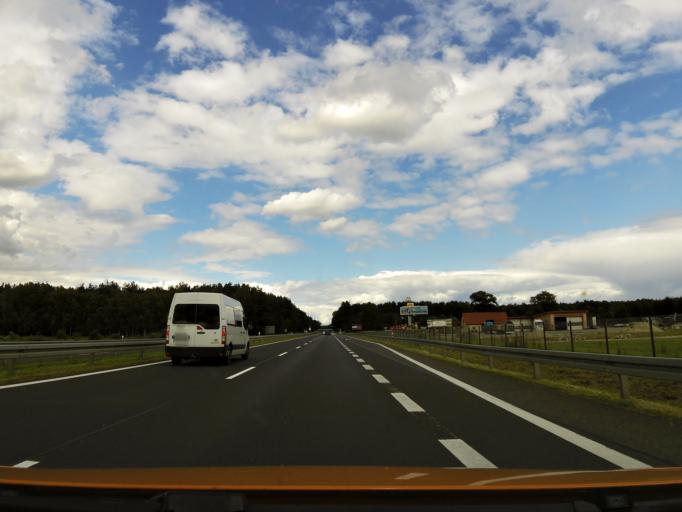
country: PL
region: West Pomeranian Voivodeship
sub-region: Powiat goleniowski
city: Goleniow
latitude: 53.5794
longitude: 14.8089
